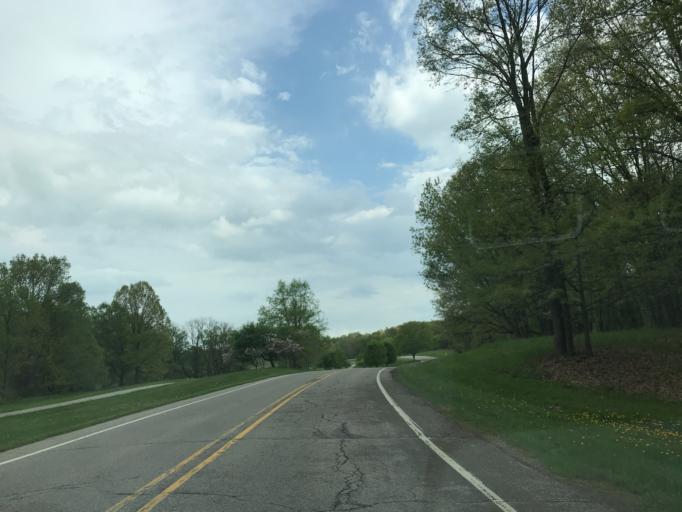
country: US
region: Michigan
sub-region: Oakland County
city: Milford
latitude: 42.5478
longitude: -83.6403
